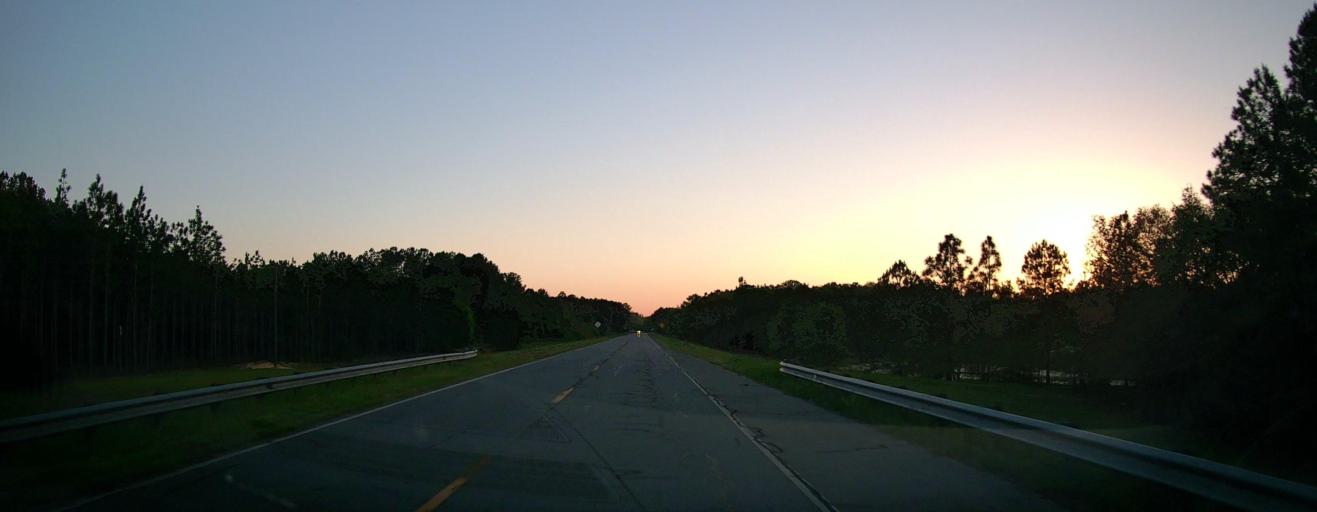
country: US
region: Georgia
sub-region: Wilcox County
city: Rochelle
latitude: 31.8175
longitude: -83.4704
